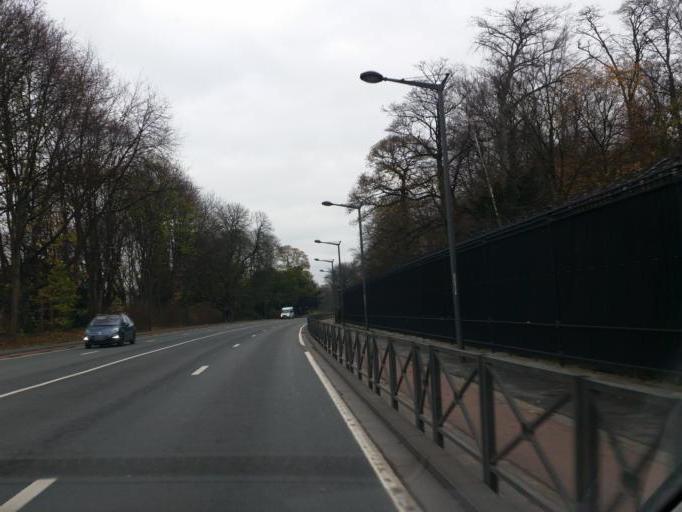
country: BE
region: Brussels Capital
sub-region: Bruxelles-Capitale
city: Brussels
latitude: 50.8857
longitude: 4.3543
